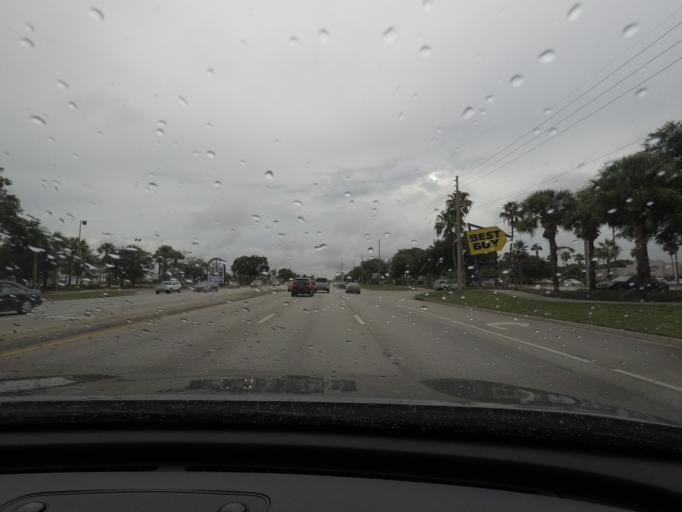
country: US
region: Florida
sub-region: Orange County
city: Azalea Park
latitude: 28.5534
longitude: -81.3283
